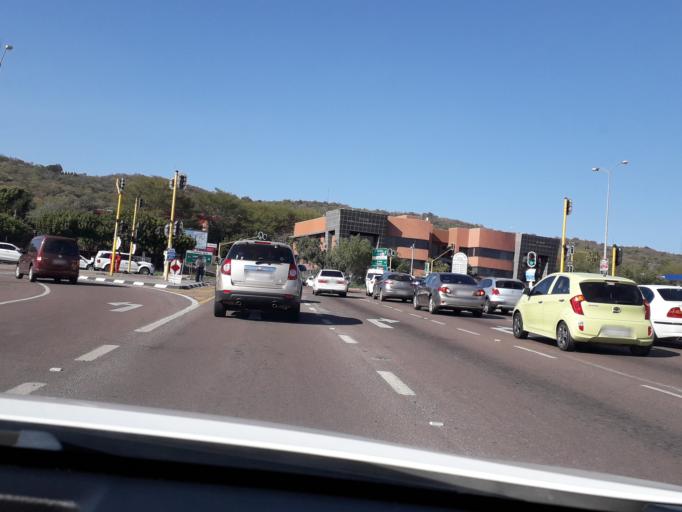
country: ZA
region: Gauteng
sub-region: City of Tshwane Metropolitan Municipality
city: Pretoria
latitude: -25.7664
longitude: 28.3216
